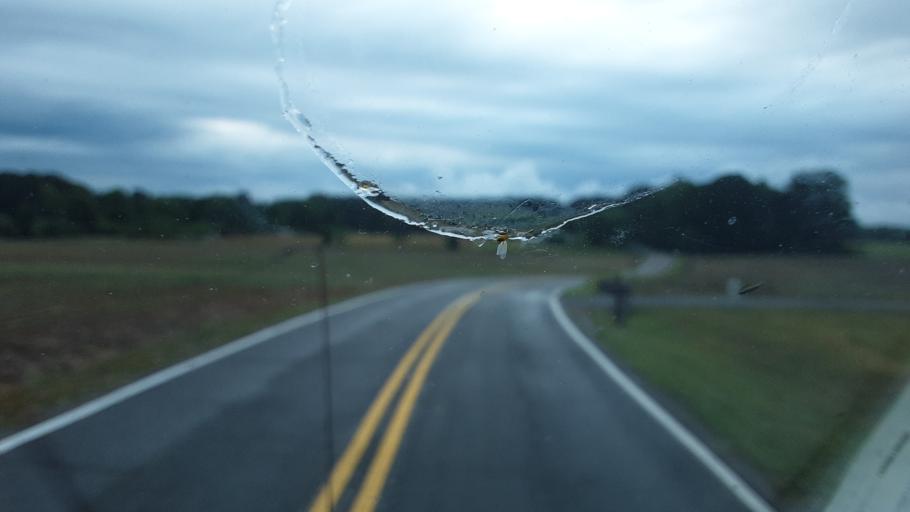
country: US
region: North Carolina
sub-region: Yadkin County
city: Jonesville
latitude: 36.0820
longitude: -80.8370
